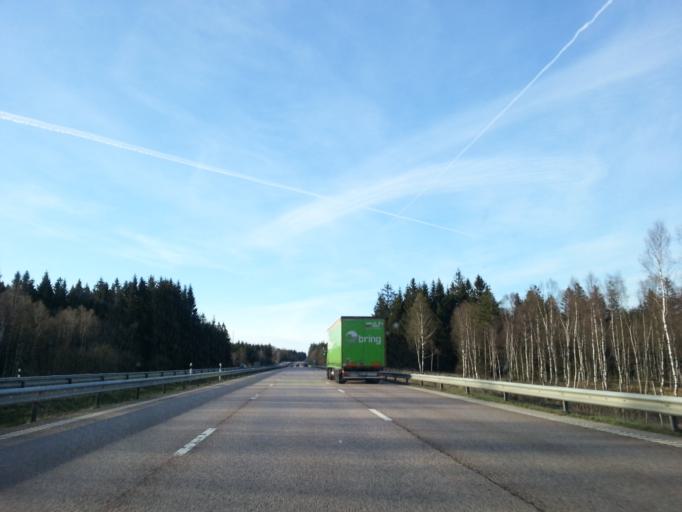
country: SE
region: Skane
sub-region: Bastads Kommun
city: Bastad
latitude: 56.3622
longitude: 12.9353
